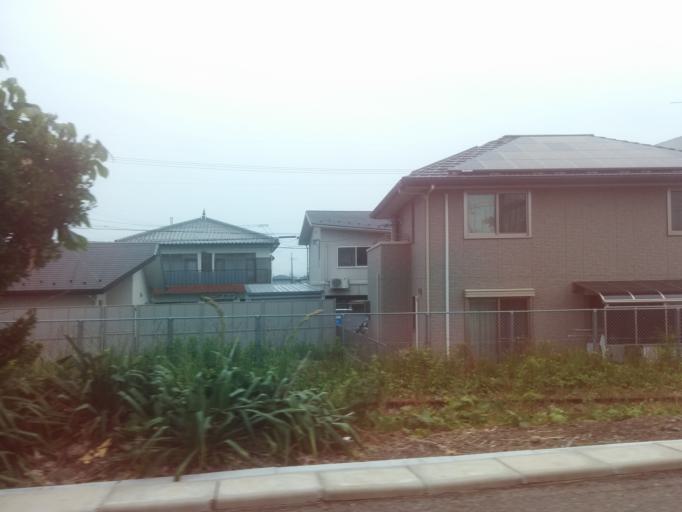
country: JP
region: Shiga Prefecture
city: Omihachiman
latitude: 35.0995
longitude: 136.0718
